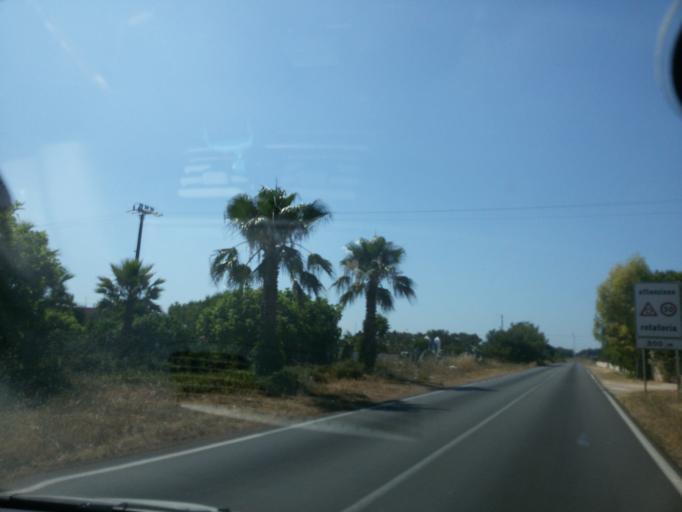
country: IT
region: Apulia
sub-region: Provincia di Lecce
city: Porto Cesareo
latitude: 40.2215
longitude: 17.9417
